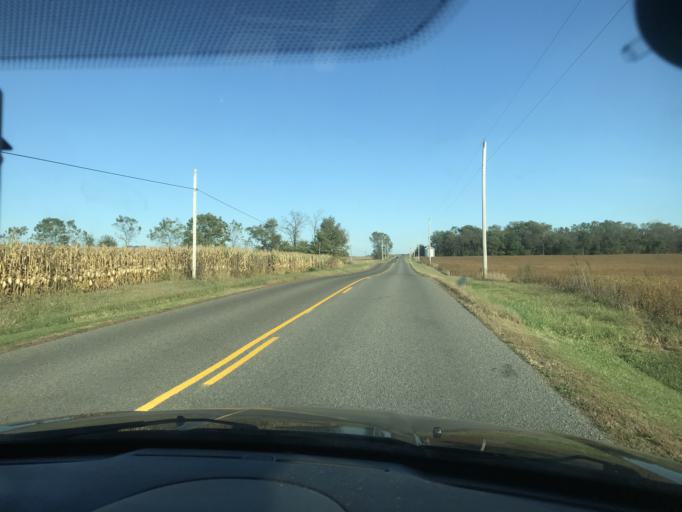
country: US
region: Ohio
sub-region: Logan County
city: Bellefontaine
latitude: 40.3212
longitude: -83.8221
